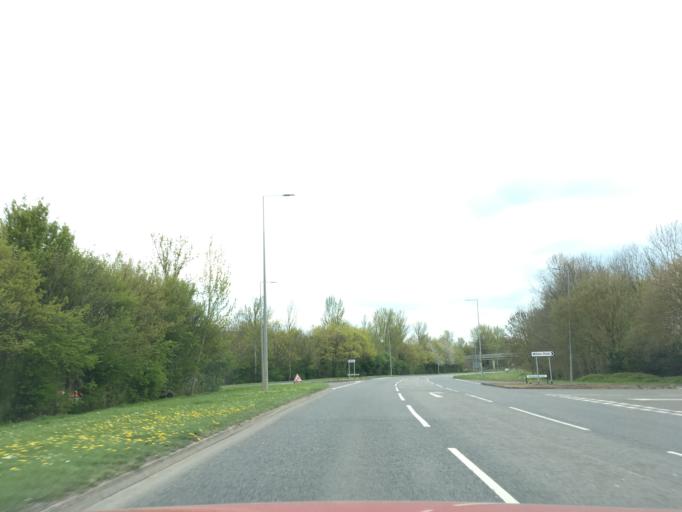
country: GB
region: England
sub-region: Milton Keynes
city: Newport Pagnell
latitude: 52.0605
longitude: -0.7303
